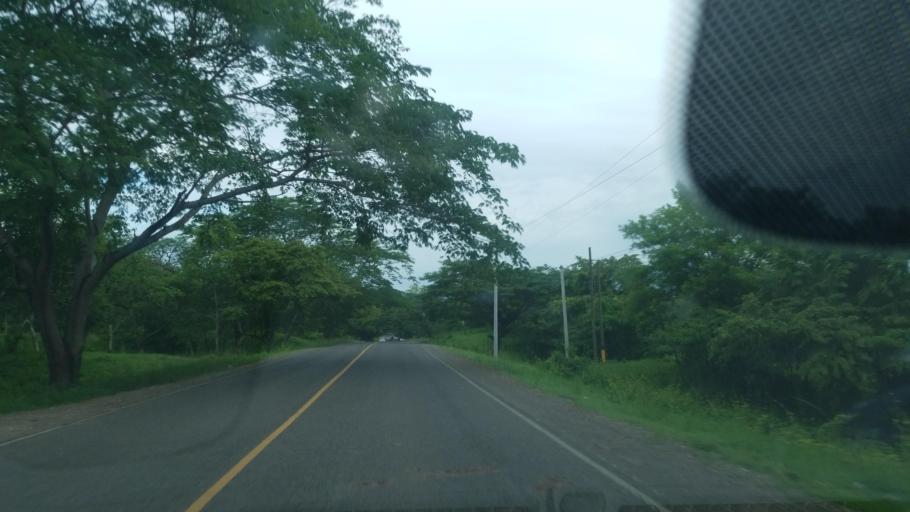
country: HN
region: Santa Barbara
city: Santa Barbara
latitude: 14.8877
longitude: -88.2487
